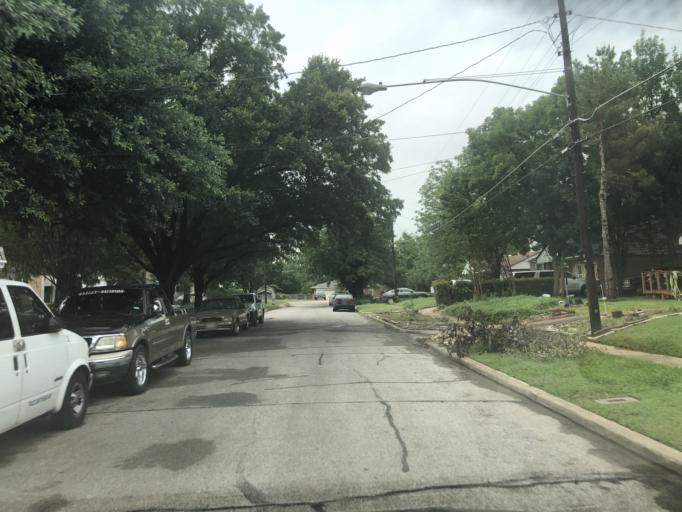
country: US
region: Texas
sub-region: Dallas County
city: Irving
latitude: 32.8041
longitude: -96.9414
